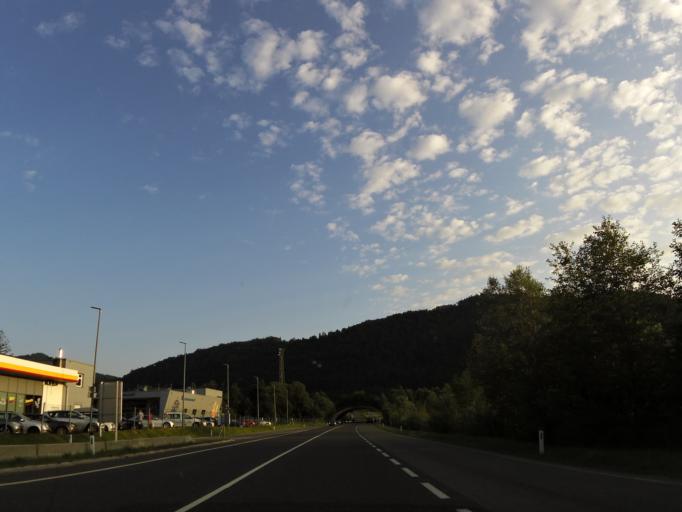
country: AT
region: Tyrol
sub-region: Politischer Bezirk Reutte
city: Musau
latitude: 47.5500
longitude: 10.6583
